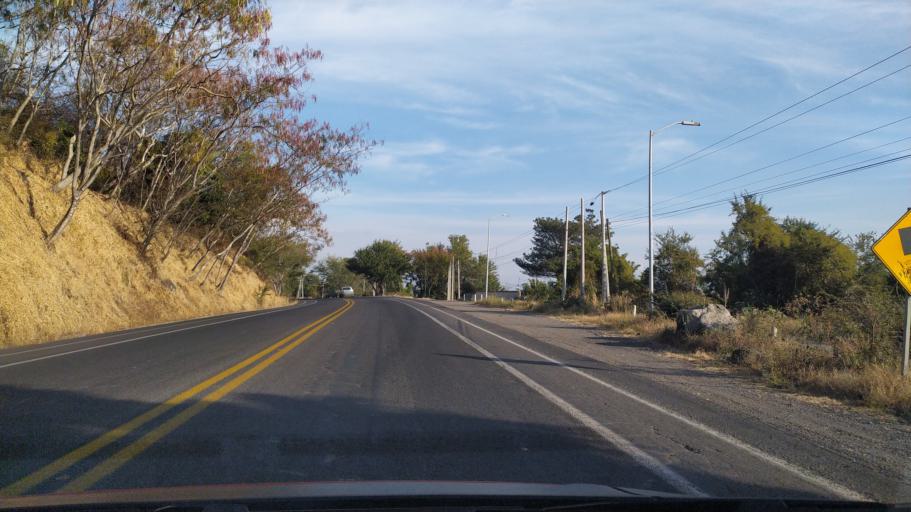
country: MX
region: Jalisco
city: Jamay
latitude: 20.2938
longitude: -102.7458
